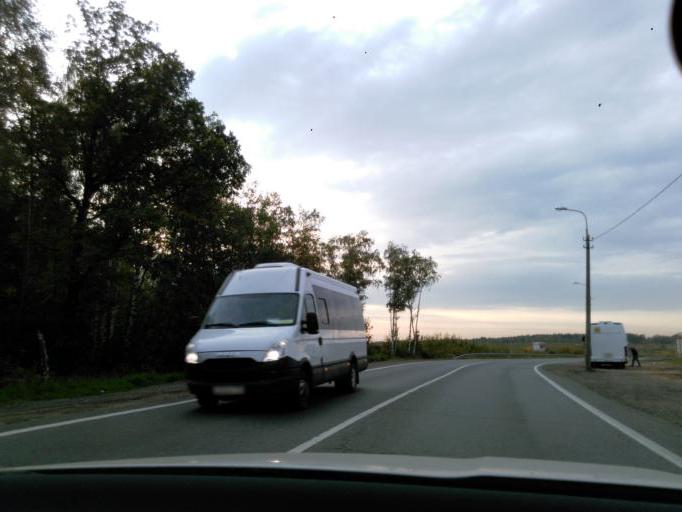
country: RU
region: Moskovskaya
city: Lobnya
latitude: 55.9822
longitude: 37.4507
